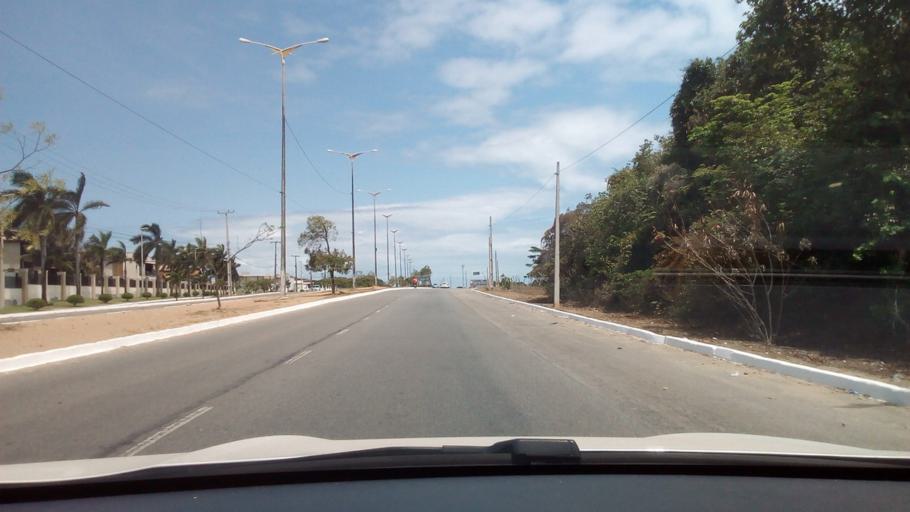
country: BR
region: Paraiba
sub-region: Joao Pessoa
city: Joao Pessoa
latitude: -7.1609
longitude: -34.8066
